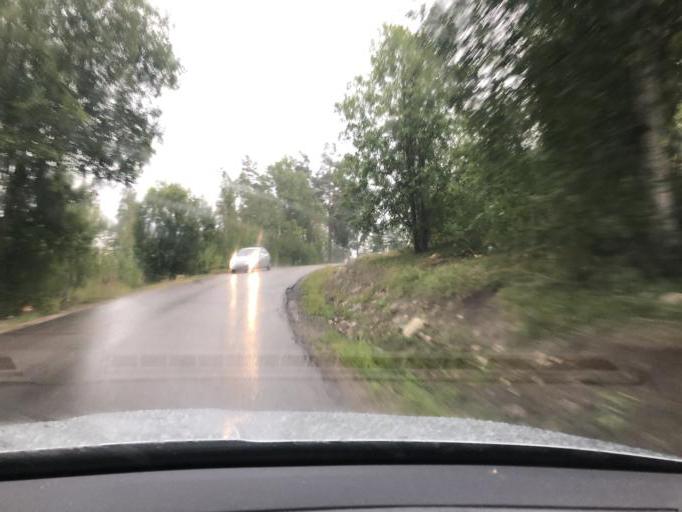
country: SE
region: Vaesternorrland
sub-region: Sundsvalls Kommun
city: Sundsvall
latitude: 62.4054
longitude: 17.3032
